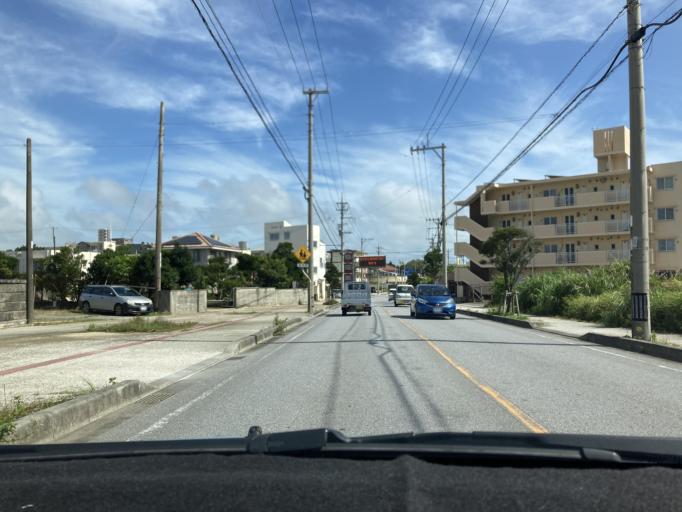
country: JP
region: Okinawa
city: Itoman
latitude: 26.1197
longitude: 127.7403
